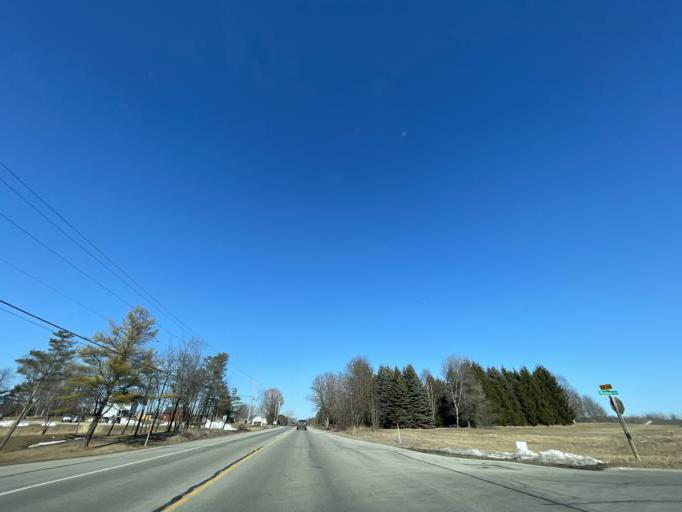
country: US
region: Wisconsin
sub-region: Brown County
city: Suamico
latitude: 44.6171
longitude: -88.0675
